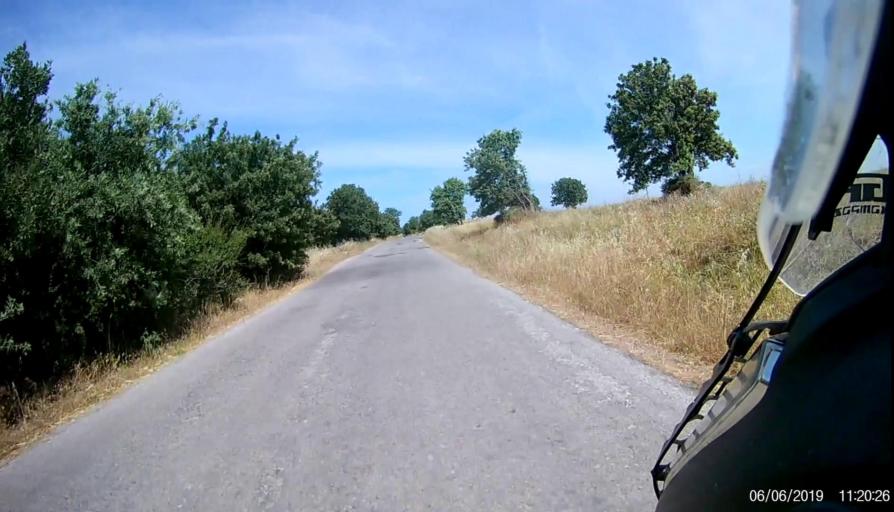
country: TR
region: Canakkale
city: Gulpinar
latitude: 39.6664
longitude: 26.1635
